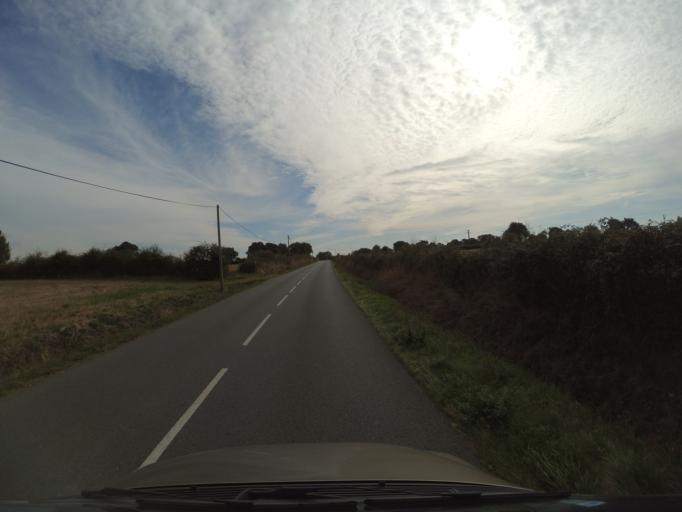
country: FR
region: Pays de la Loire
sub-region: Departement de Maine-et-Loire
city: Melay
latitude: 47.2087
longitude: -0.6726
